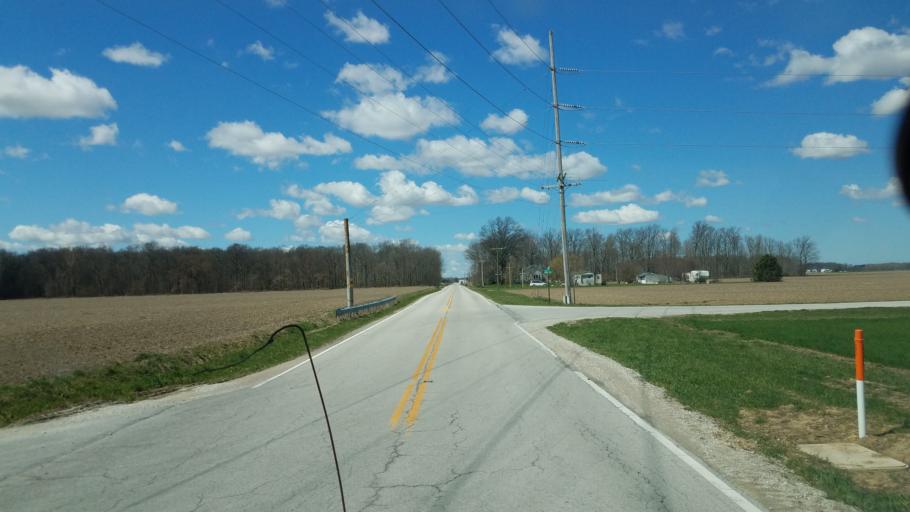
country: US
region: Ohio
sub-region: Sandusky County
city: Green Springs
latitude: 41.2567
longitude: -83.1117
